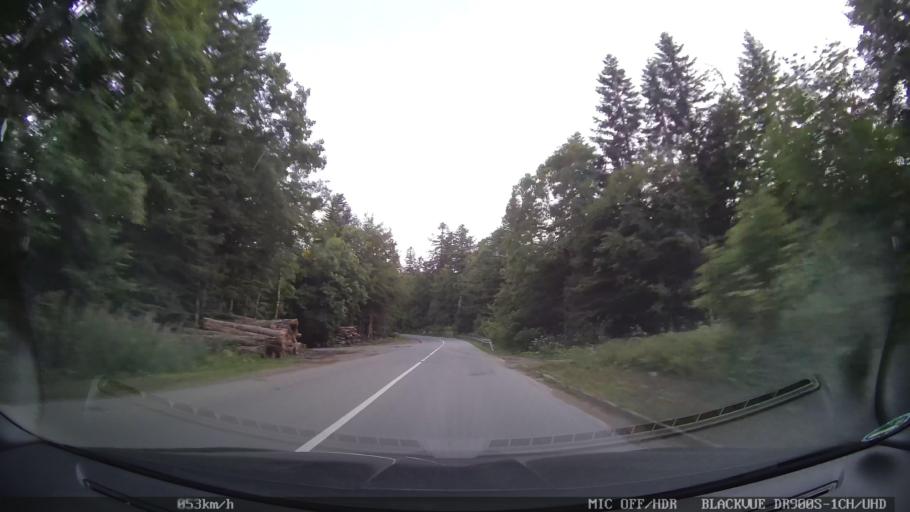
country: HR
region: Primorsko-Goranska
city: Novi Vinodolski
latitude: 45.1734
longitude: 14.9735
